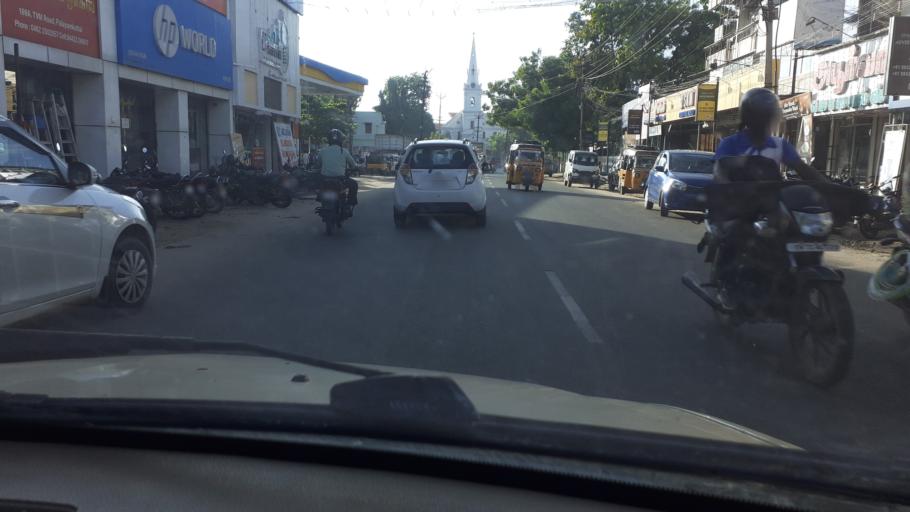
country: IN
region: Tamil Nadu
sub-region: Tirunelveli Kattabo
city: Tirunelveli
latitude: 8.7264
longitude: 77.7292
